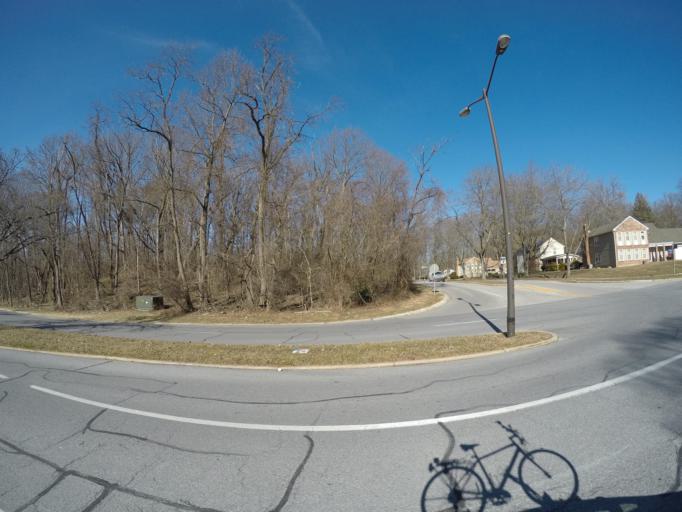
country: US
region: Maryland
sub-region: Howard County
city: Columbia
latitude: 39.2204
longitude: -76.8373
